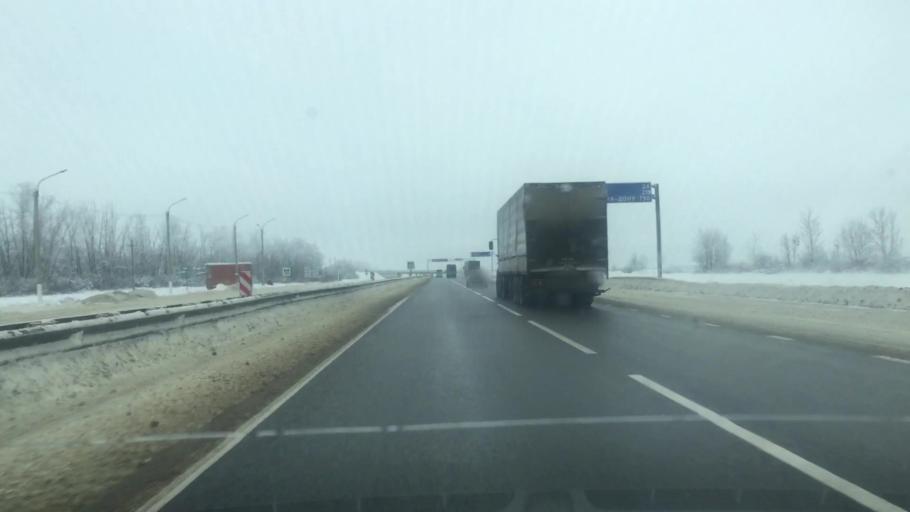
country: RU
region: Tula
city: Kazachka
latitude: 53.3054
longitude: 38.1786
